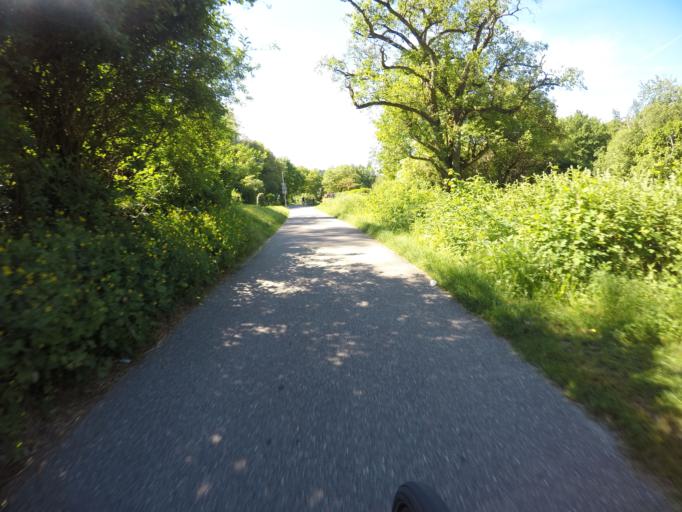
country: DE
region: Baden-Wuerttemberg
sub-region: Karlsruhe Region
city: Konigsbach-Stein
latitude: 48.9377
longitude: 8.6306
